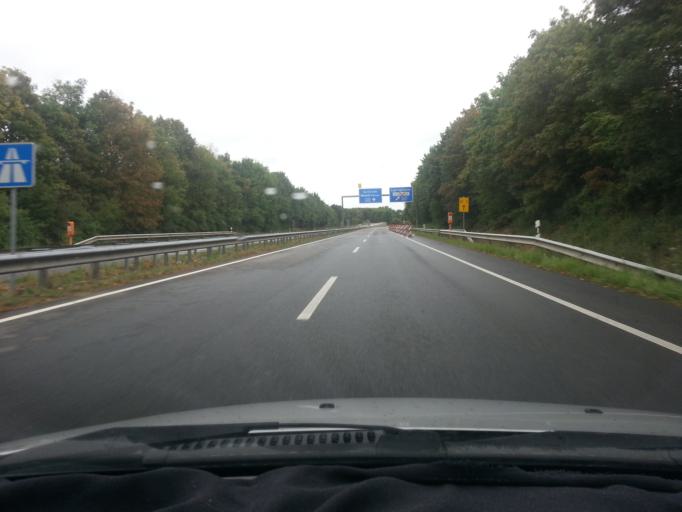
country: DE
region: Rheinland-Pfalz
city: Ruppertsberg
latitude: 49.3830
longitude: 8.2163
